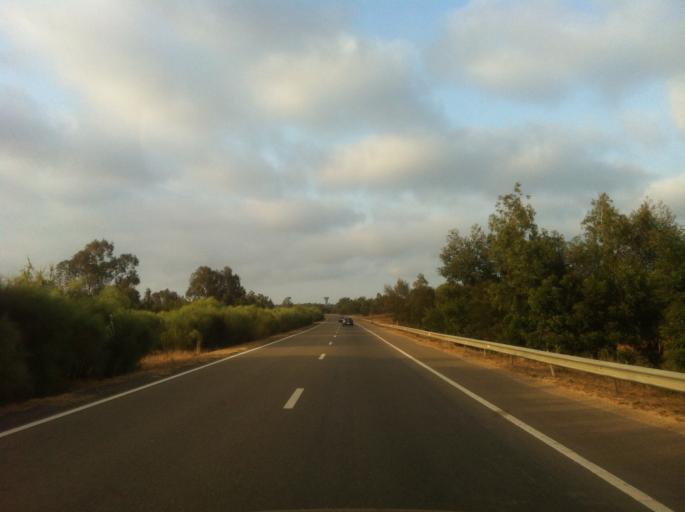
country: MA
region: Gharb-Chrarda-Beni Hssen
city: Sidi Yahia el Gharb
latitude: 34.6467
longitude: -6.4048
